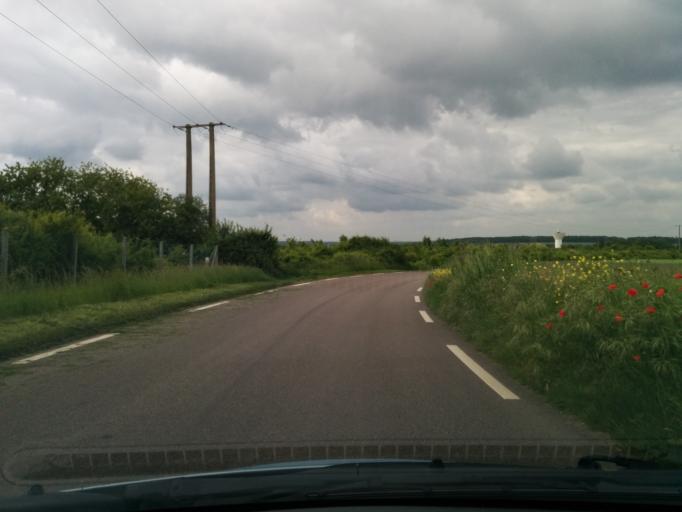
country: FR
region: Ile-de-France
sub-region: Departement des Yvelines
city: Issou
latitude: 49.0146
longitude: 1.7880
